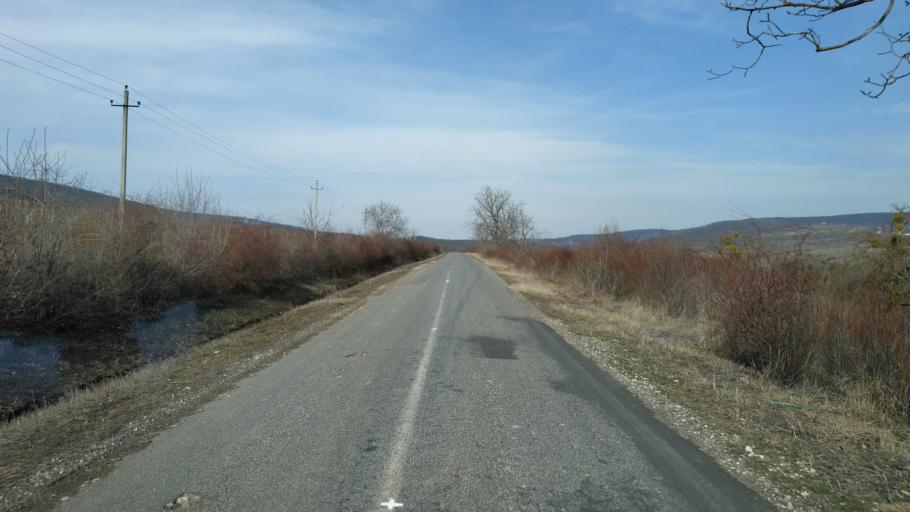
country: MD
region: Nisporeni
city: Nisporeni
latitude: 47.1743
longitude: 28.0874
